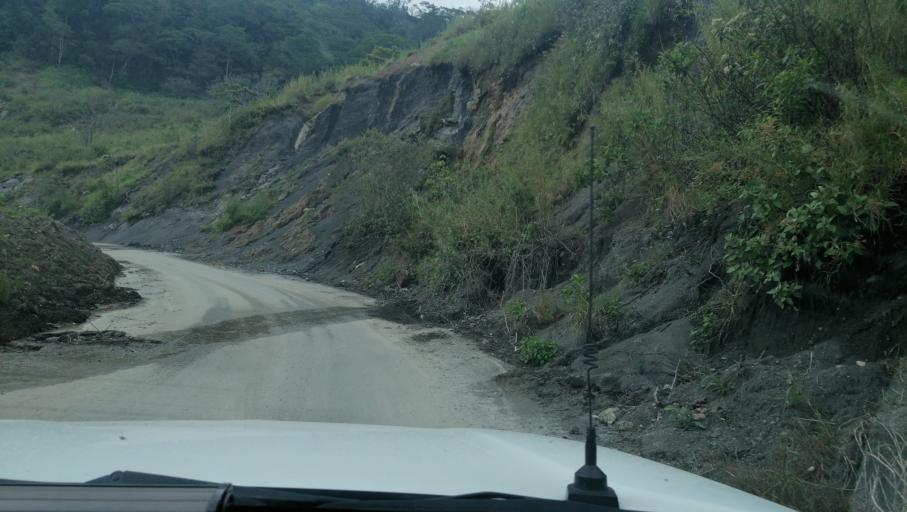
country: MX
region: Chiapas
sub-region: Ocotepec
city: San Pablo Huacano
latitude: 17.2638
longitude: -93.2658
